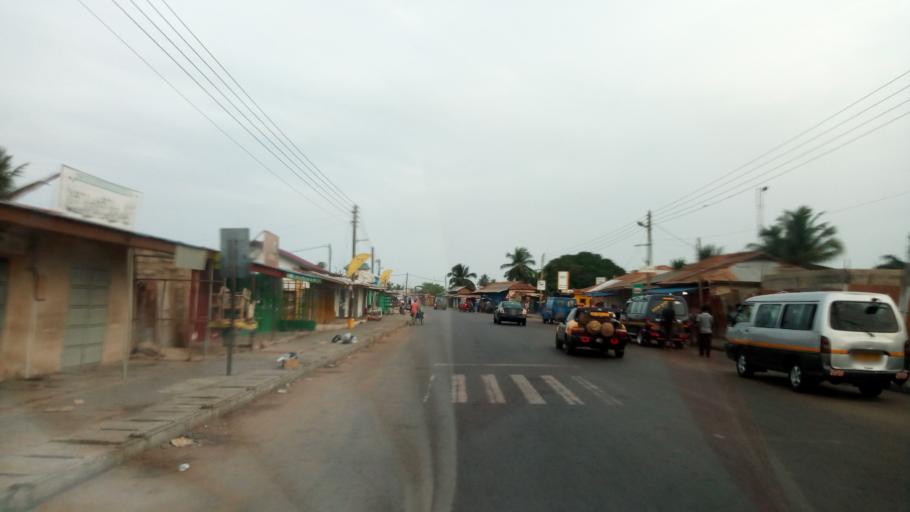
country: TG
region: Maritime
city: Lome
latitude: 6.1195
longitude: 1.1879
